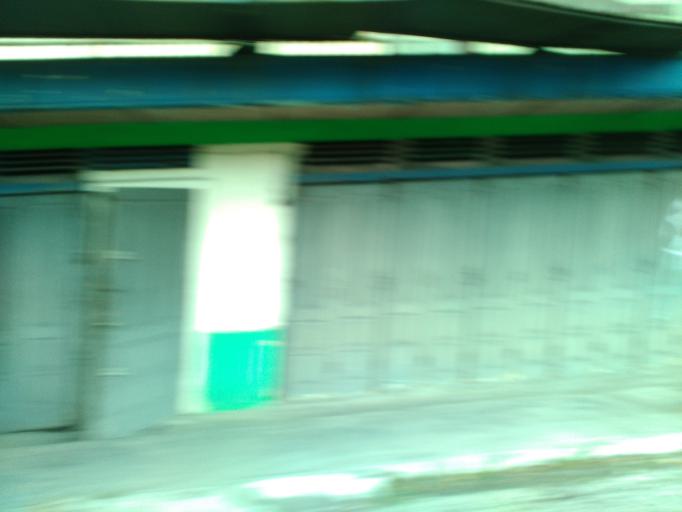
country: ID
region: Central Java
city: Ceper
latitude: -7.6791
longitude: 110.6502
